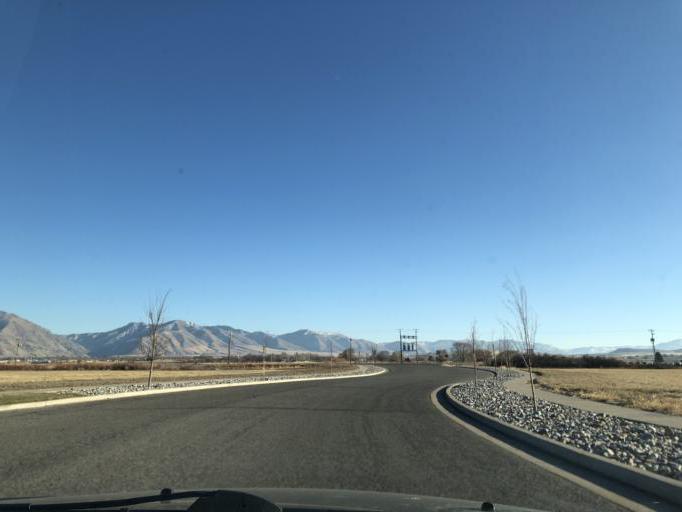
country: US
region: Utah
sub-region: Cache County
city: Wellsville
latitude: 41.6503
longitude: -111.9112
